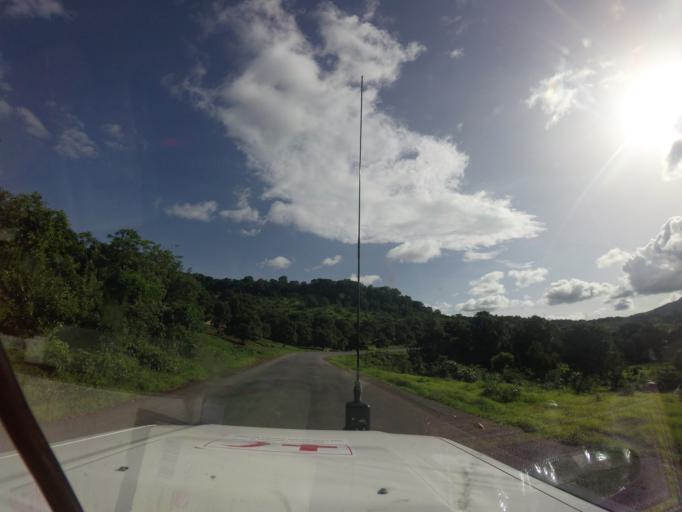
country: GN
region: Kindia
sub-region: Kindia
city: Kindia
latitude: 10.1790
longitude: -12.4731
